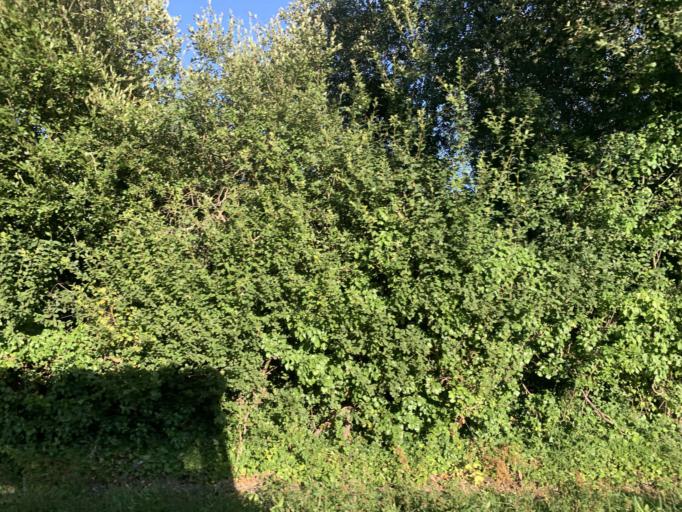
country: FR
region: Pays de la Loire
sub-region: Departement de la Loire-Atlantique
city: Pornichet
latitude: 47.2539
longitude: -2.3046
